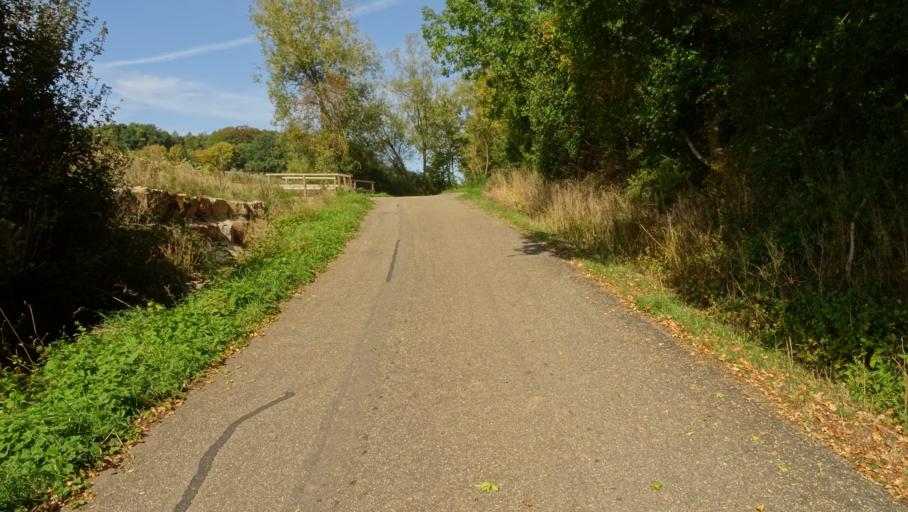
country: DE
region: Baden-Wuerttemberg
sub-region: Karlsruhe Region
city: Mosbach
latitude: 49.3795
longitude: 9.1633
